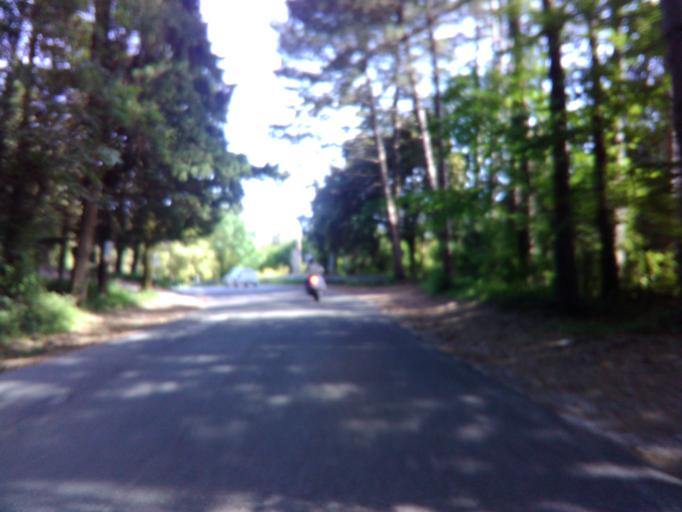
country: IT
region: Tuscany
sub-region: Provincia di Massa-Carrara
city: Fosdinovo
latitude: 44.1395
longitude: 10.0228
